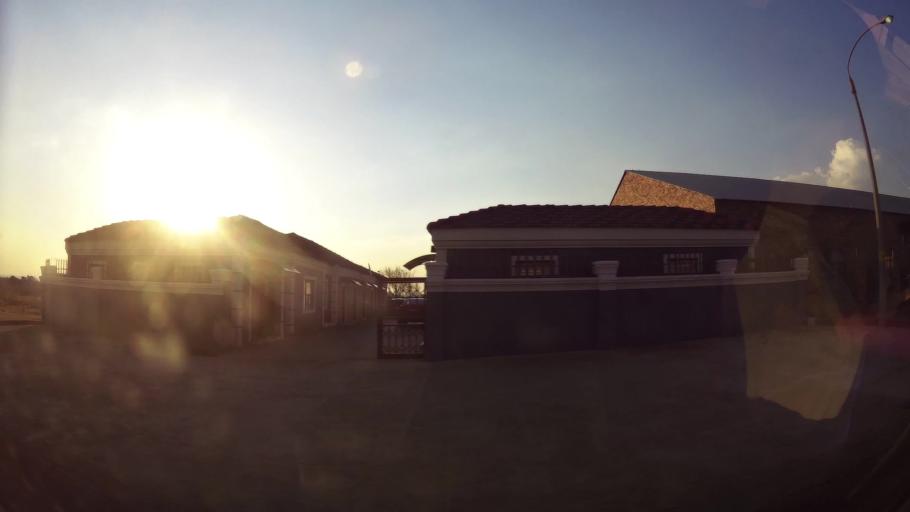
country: ZA
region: Gauteng
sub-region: Ekurhuleni Metropolitan Municipality
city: Germiston
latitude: -26.3075
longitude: 28.2374
